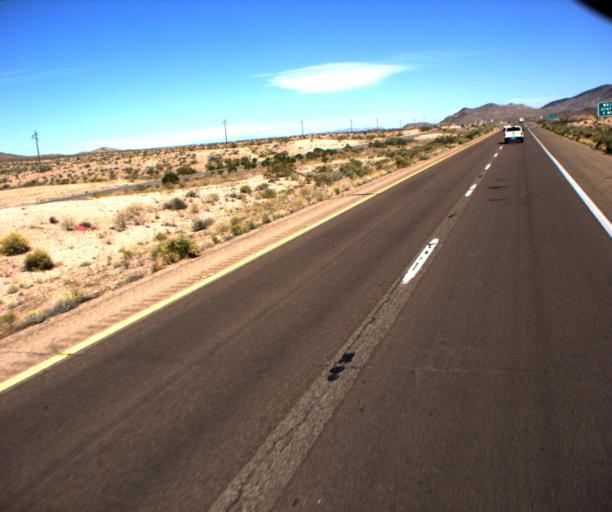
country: US
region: Nevada
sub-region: Clark County
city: Boulder City
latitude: 35.8176
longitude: -114.5501
